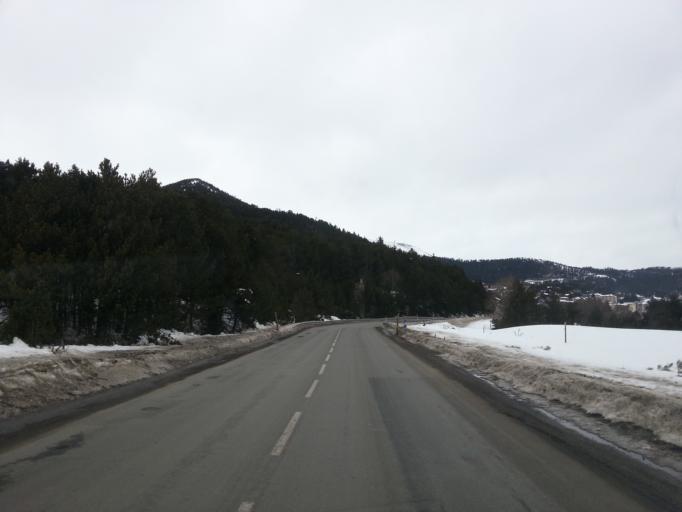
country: ES
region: Catalonia
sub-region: Provincia de Girona
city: Llivia
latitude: 42.5613
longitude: 2.0755
